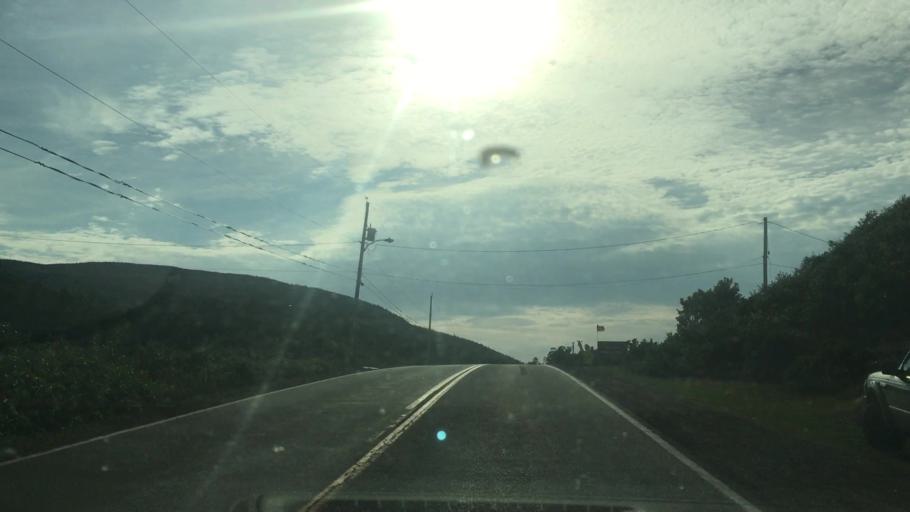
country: CA
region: Nova Scotia
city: Sydney Mines
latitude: 46.8243
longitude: -60.8189
